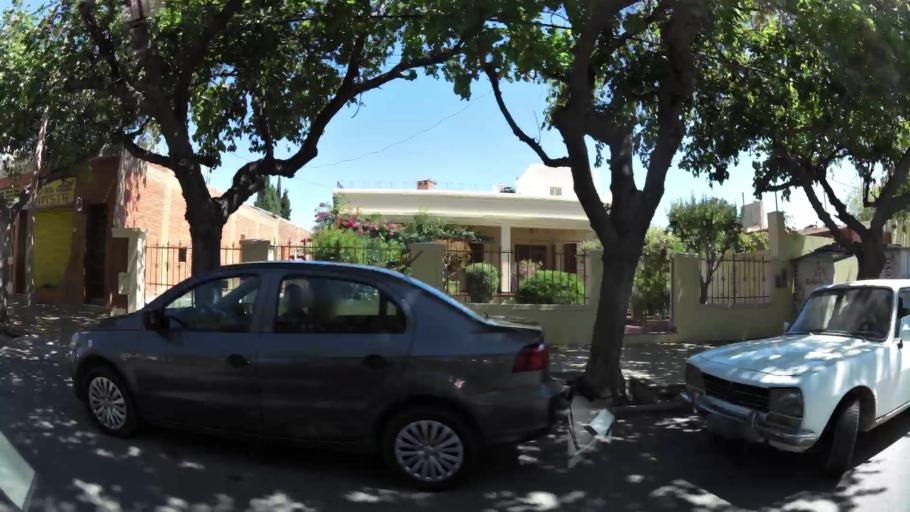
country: AR
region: San Juan
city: San Juan
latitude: -31.5267
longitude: -68.5225
